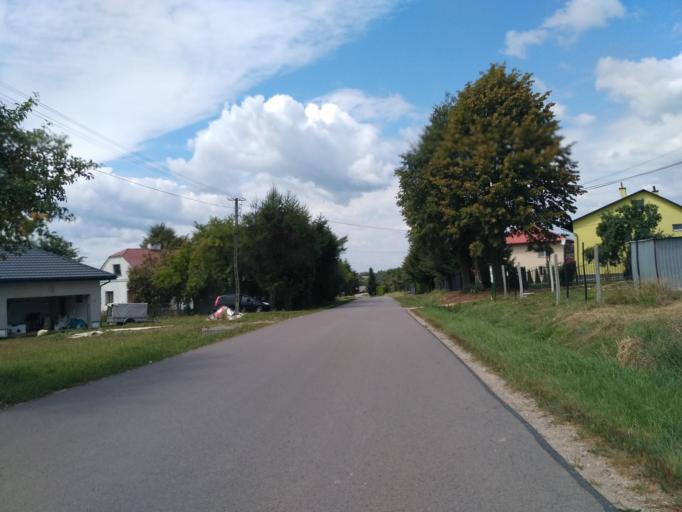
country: PL
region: Subcarpathian Voivodeship
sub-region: Powiat rzeszowski
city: Hyzne
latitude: 49.9219
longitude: 22.2023
